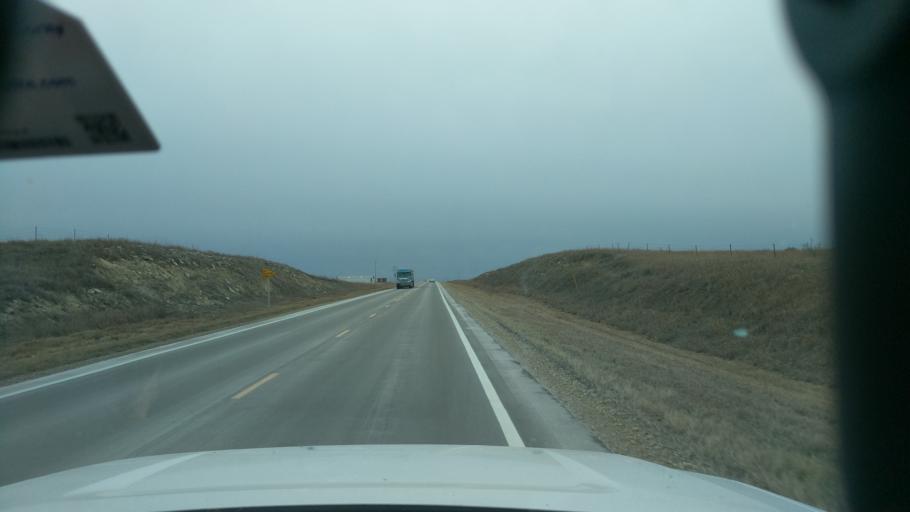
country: US
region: Kansas
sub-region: Dickinson County
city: Herington
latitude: 38.6882
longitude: -96.9305
